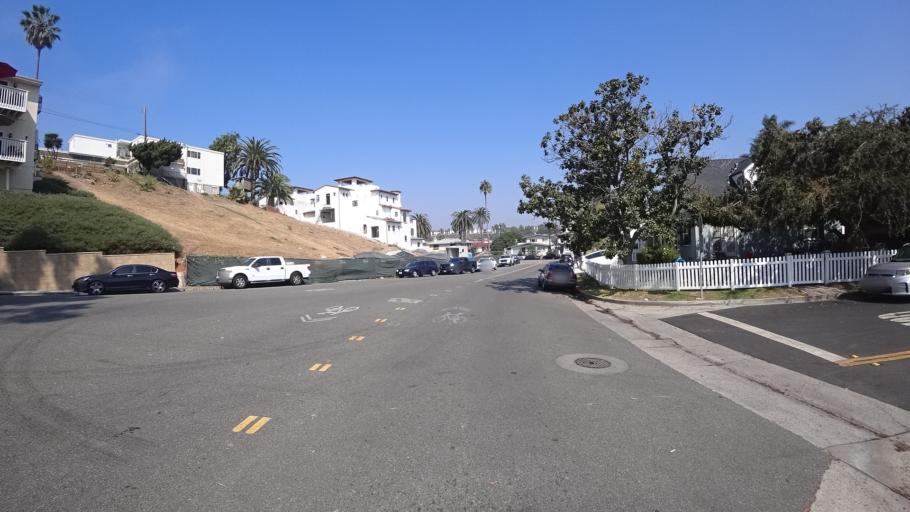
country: US
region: California
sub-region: Orange County
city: San Clemente
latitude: 33.4311
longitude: -117.6291
